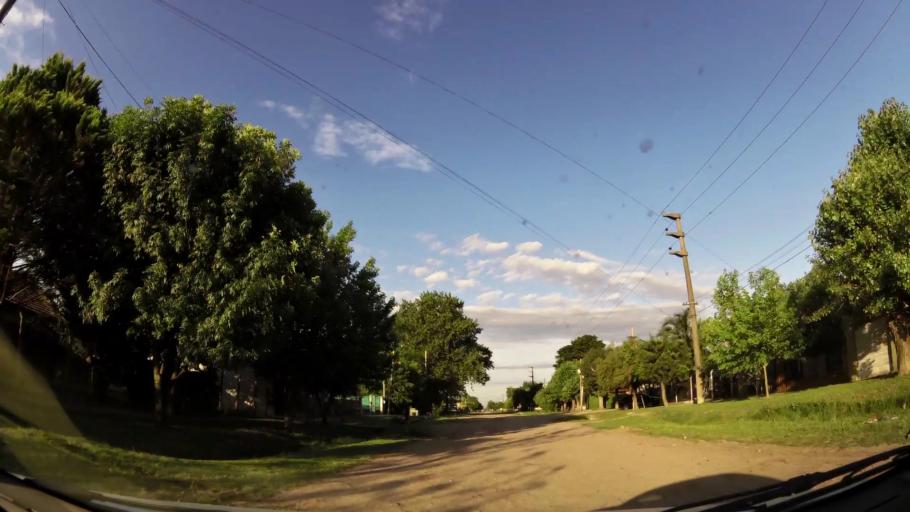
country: AR
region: Buenos Aires
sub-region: Partido de Merlo
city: Merlo
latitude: -34.6941
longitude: -58.7503
